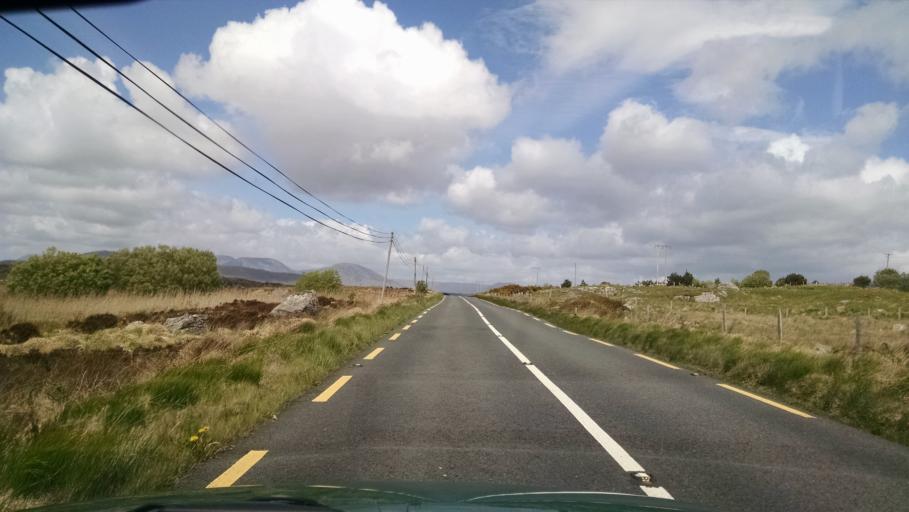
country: IE
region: Connaught
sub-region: County Galway
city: Oughterard
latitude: 53.3609
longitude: -9.5428
